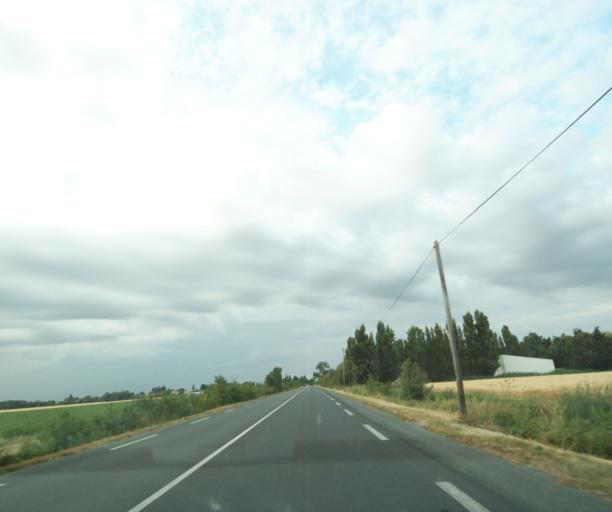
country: FR
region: Pays de la Loire
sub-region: Departement de la Vendee
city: Chaille-les-Marais
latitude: 46.3598
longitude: -0.9906
